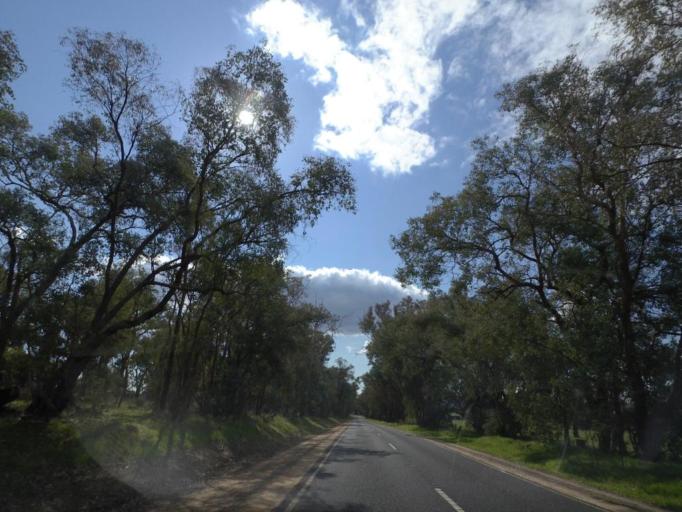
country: AU
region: New South Wales
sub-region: Corowa Shire
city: Howlong
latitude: -36.2339
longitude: 146.6307
